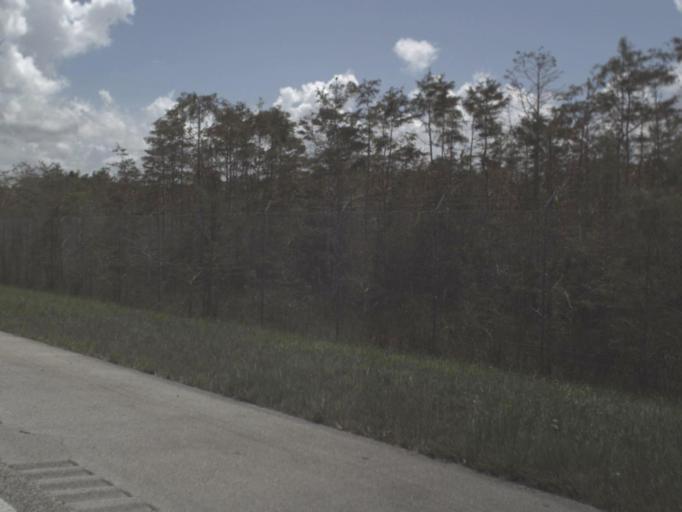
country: US
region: Florida
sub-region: Collier County
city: Immokalee
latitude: 26.1678
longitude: -81.1242
